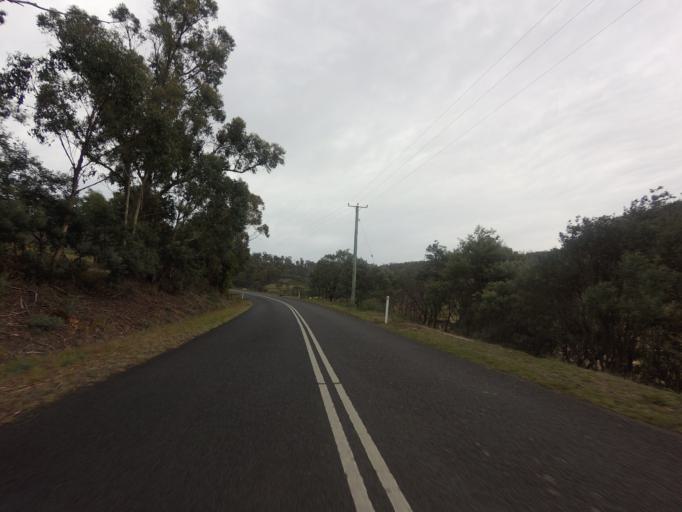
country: AU
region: Tasmania
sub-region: Derwent Valley
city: New Norfolk
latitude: -42.5929
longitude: 147.0377
